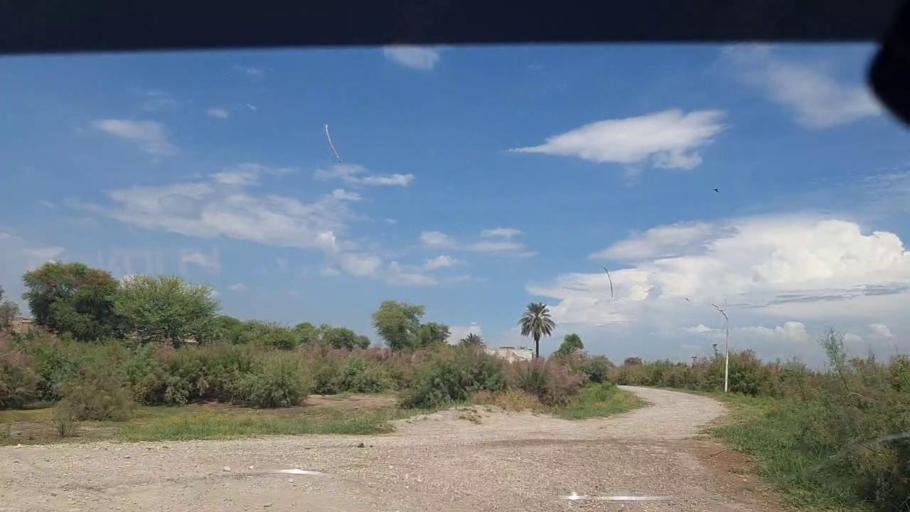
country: PK
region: Sindh
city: Ghauspur
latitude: 28.1442
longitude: 68.9820
